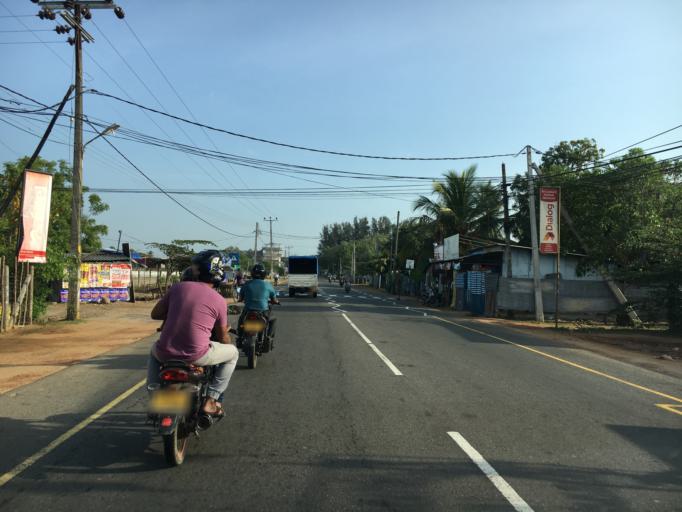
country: LK
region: Eastern Province
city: Eravur Town
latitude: 7.9024
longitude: 81.5351
